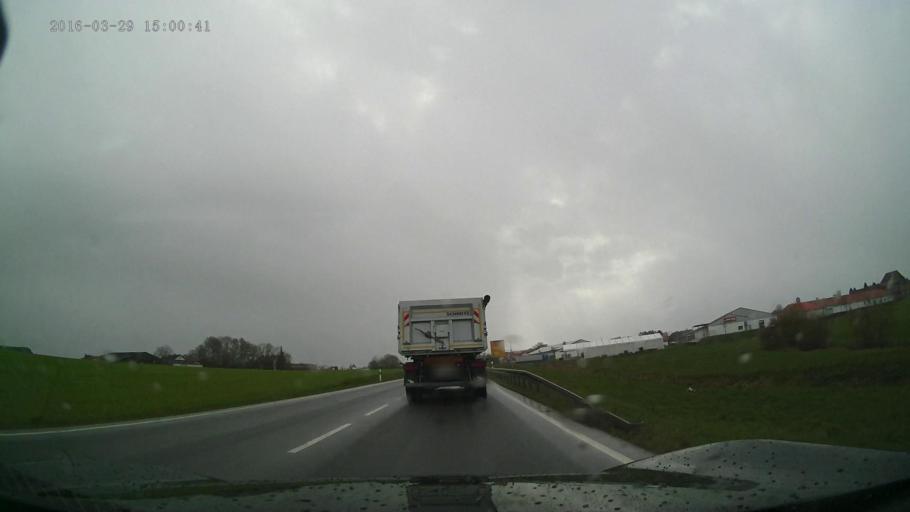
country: DE
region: Baden-Wuerttemberg
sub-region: Karlsruhe Region
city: Walldurn
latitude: 49.5768
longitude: 9.3736
